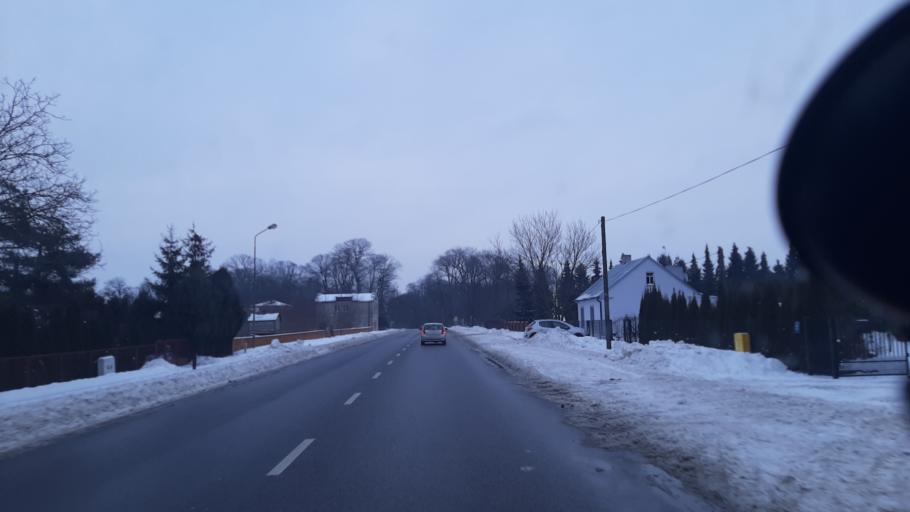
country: PL
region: Lublin Voivodeship
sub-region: Powiat lubelski
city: Garbow
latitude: 51.3559
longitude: 22.3267
